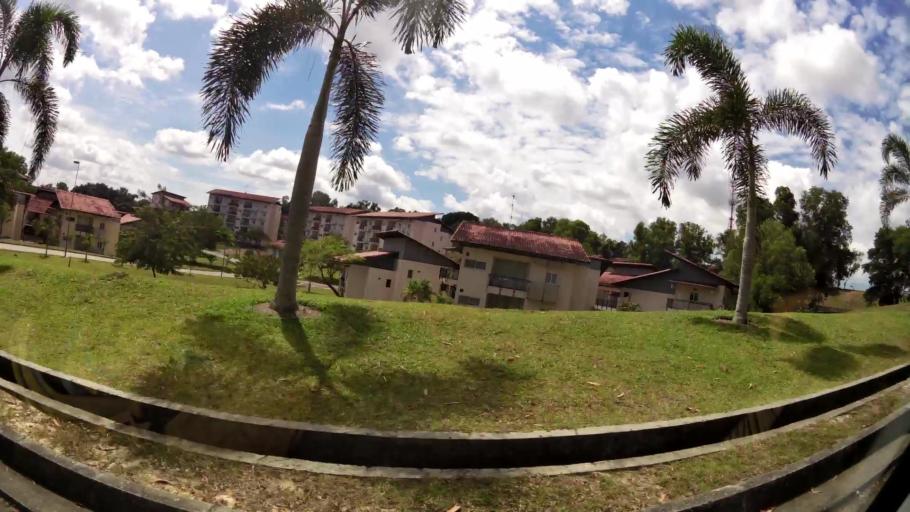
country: BN
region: Brunei and Muara
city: Bandar Seri Begawan
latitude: 4.9339
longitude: 114.8898
